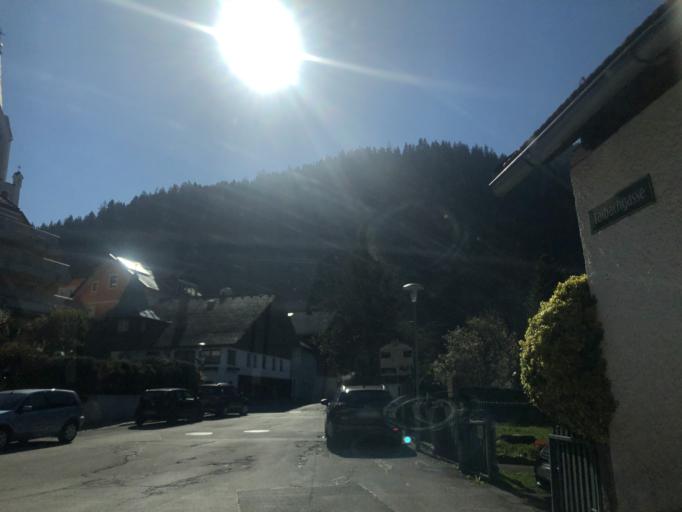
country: AT
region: Styria
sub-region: Politischer Bezirk Liezen
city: Schladming
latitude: 47.3904
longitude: 13.6874
